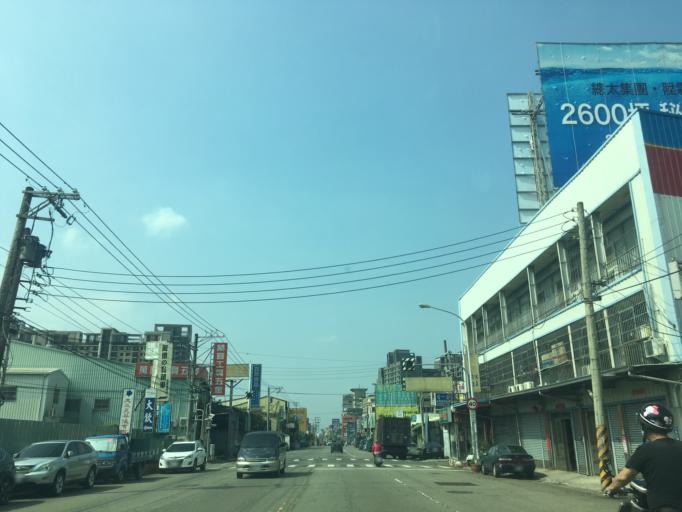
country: TW
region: Taiwan
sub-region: Taichung City
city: Taichung
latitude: 24.1627
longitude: 120.7141
